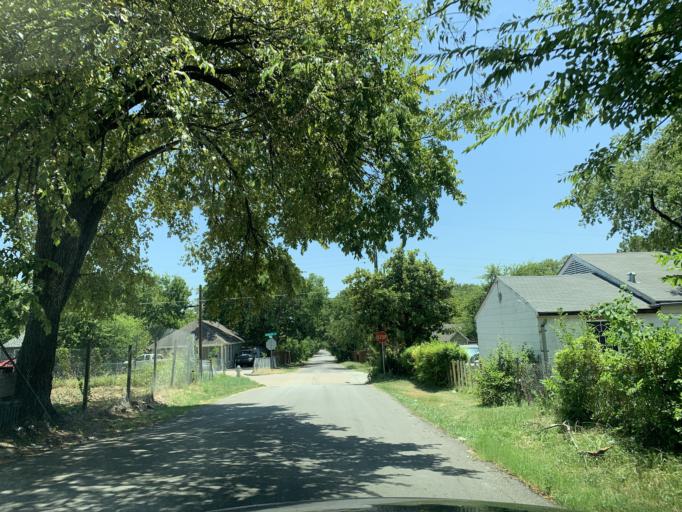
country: US
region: Texas
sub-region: Dallas County
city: Dallas
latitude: 32.6878
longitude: -96.8011
